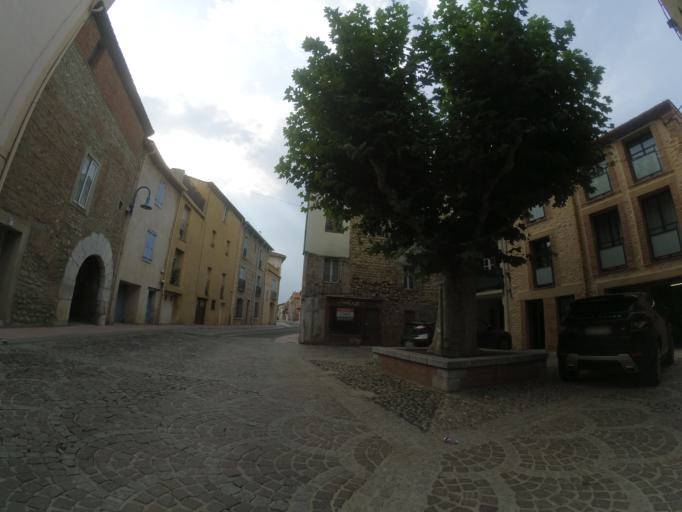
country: FR
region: Languedoc-Roussillon
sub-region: Departement des Pyrenees-Orientales
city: Corneilla-la-Riviere
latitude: 42.6821
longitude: 2.7367
